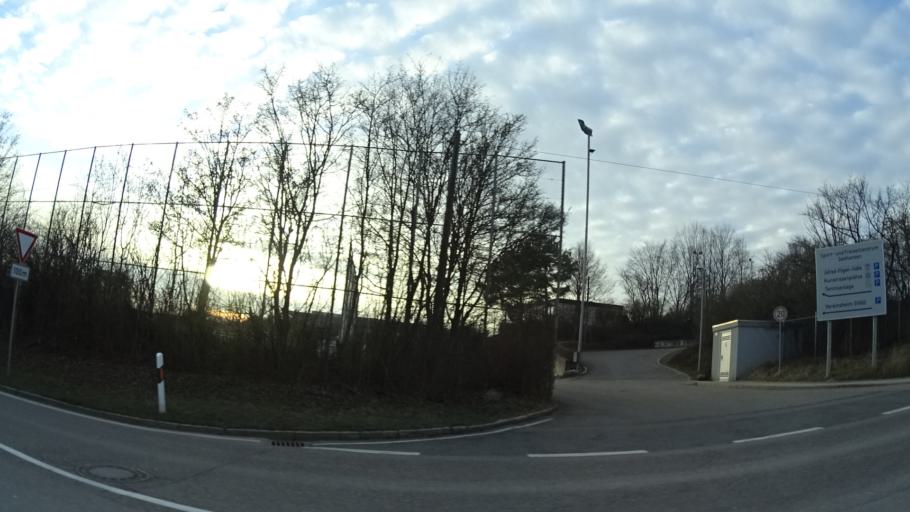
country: DE
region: Baden-Wuerttemberg
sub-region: Regierungsbezirk Stuttgart
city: Hemmingen
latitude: 48.8387
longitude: 9.0308
